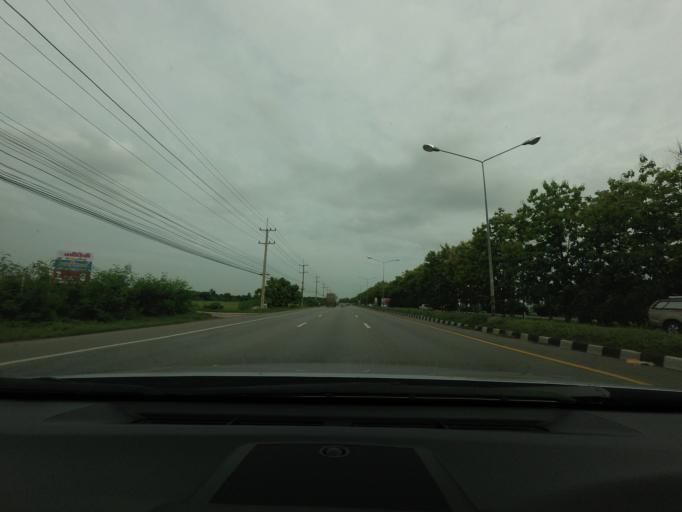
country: TH
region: Phetchaburi
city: Khao Yoi
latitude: 13.1859
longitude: 99.8343
